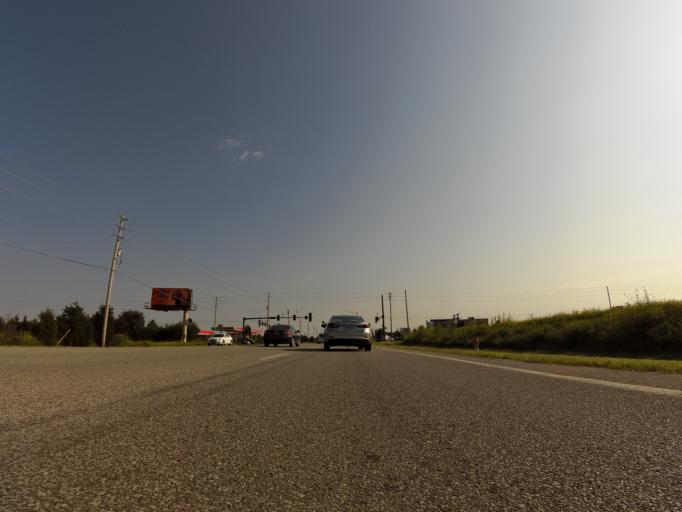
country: US
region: Kansas
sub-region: Sedgwick County
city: Maize
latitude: 37.7531
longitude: -97.4264
